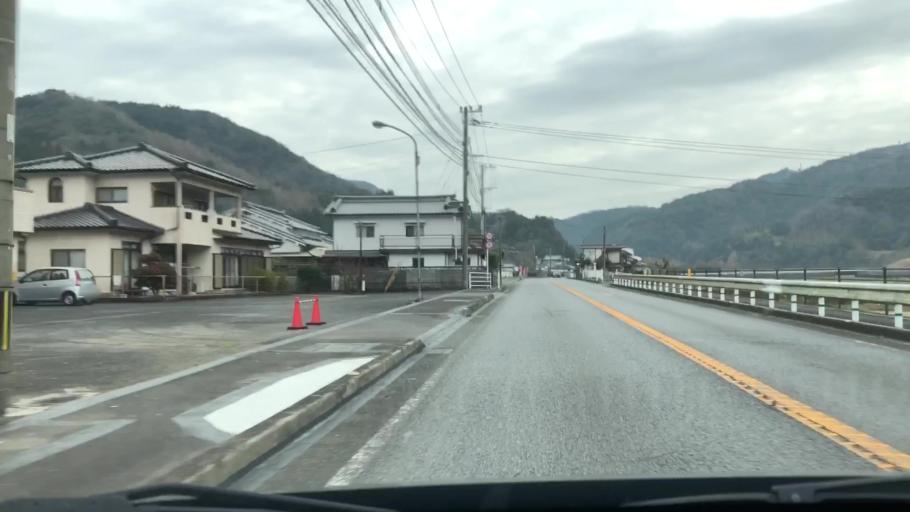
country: JP
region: Oita
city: Usuki
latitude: 33.0060
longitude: 131.7219
